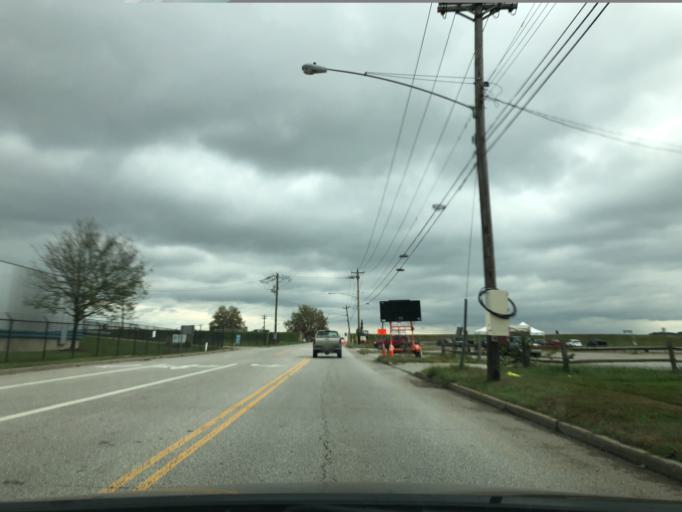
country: US
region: Kentucky
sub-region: Campbell County
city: Fort Thomas
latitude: 39.1023
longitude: -84.4320
